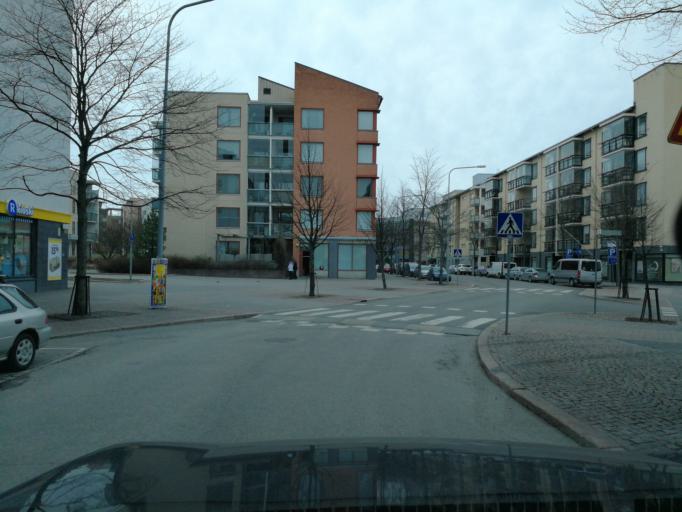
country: FI
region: Uusimaa
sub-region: Helsinki
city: Helsinki
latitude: 60.1871
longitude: 25.0359
